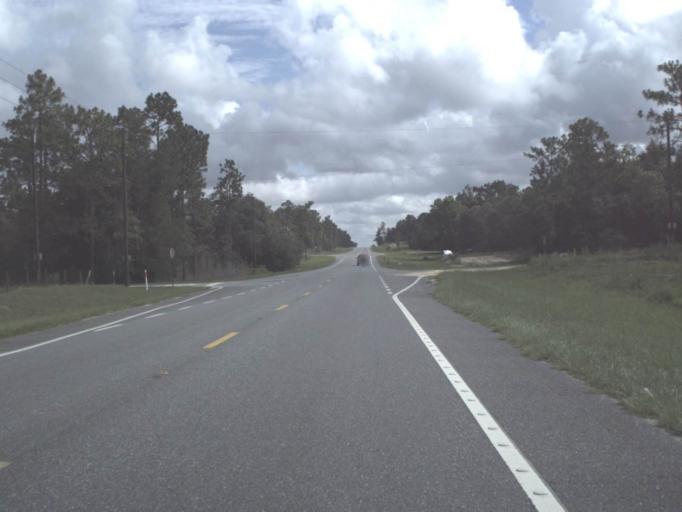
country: US
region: Florida
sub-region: Levy County
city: Williston Highlands
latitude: 29.2968
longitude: -82.5322
